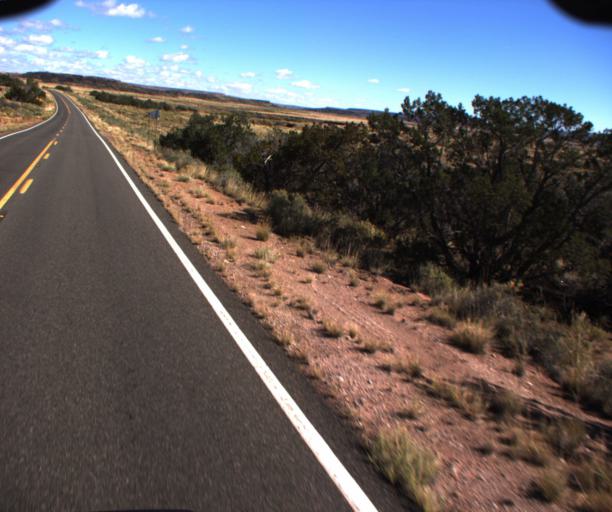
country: US
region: Arizona
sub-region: Apache County
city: Saint Johns
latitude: 34.7314
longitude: -109.2537
